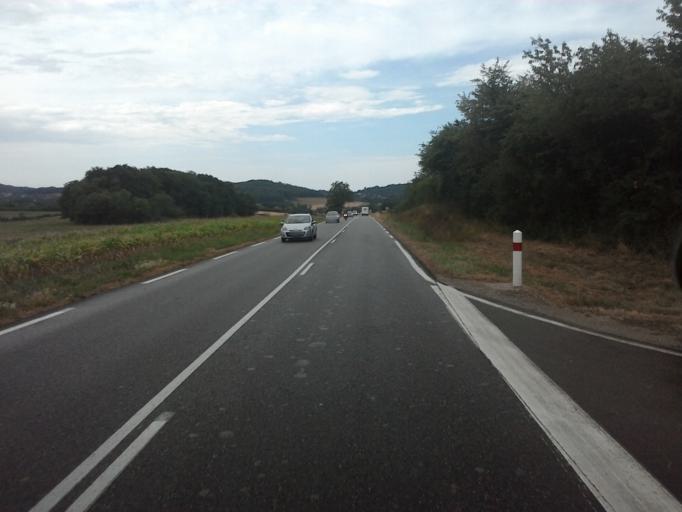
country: FR
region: Franche-Comte
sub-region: Departement du Jura
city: Poligny
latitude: 46.8237
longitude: 5.5950
